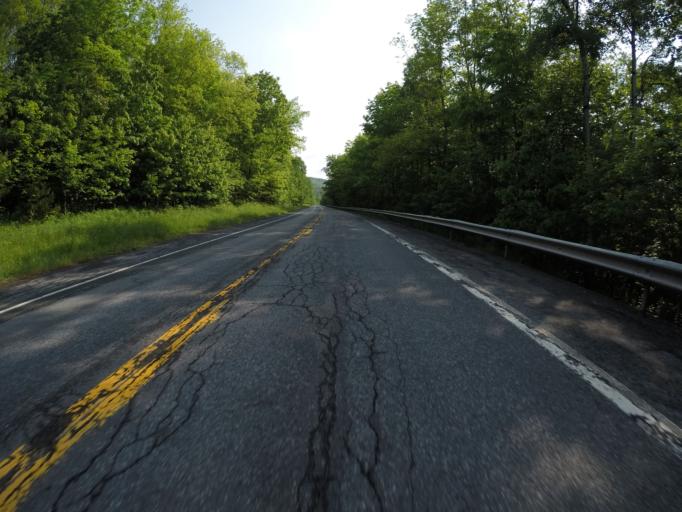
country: US
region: New York
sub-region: Sullivan County
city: Livingston Manor
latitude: 42.1212
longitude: -74.7270
